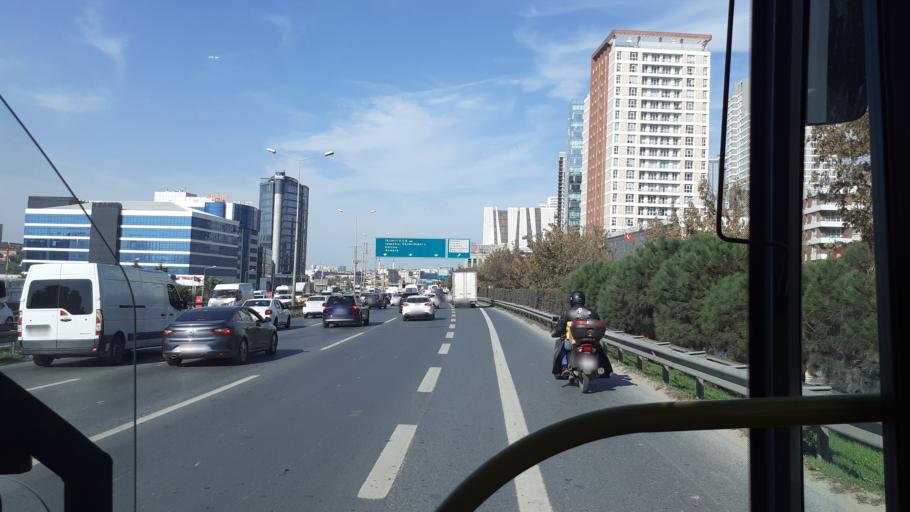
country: TR
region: Istanbul
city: Mahmutbey
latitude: 41.0382
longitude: 28.8107
